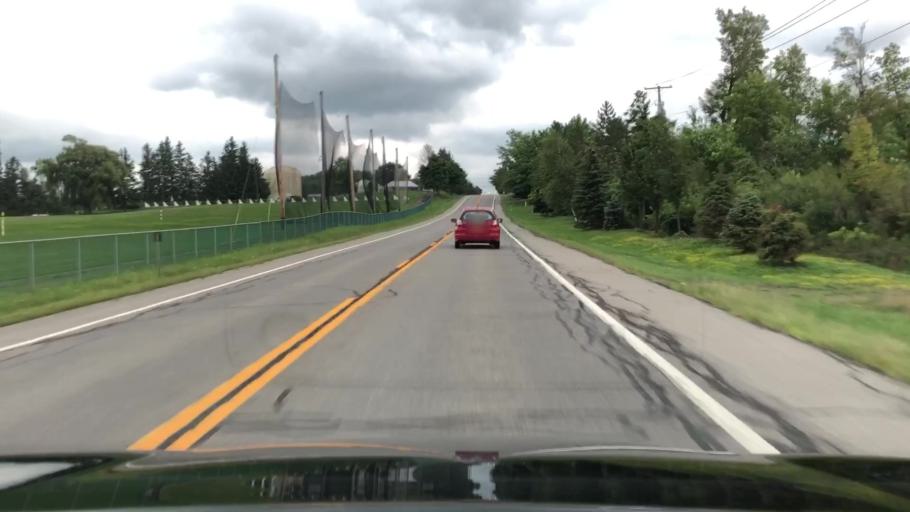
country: US
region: New York
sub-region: Erie County
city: Orchard Park
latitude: 42.7747
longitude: -78.6968
